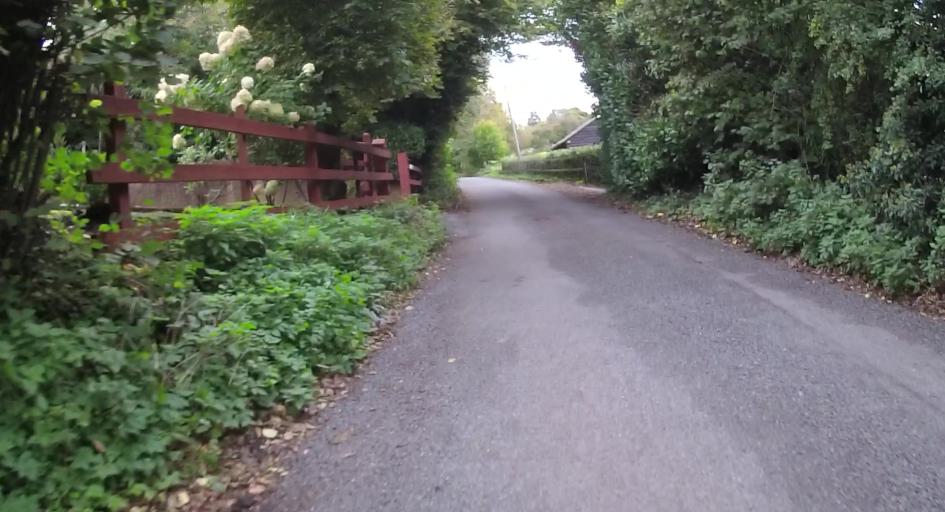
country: GB
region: England
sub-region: Hampshire
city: Four Marks
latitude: 51.0995
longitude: -1.0359
